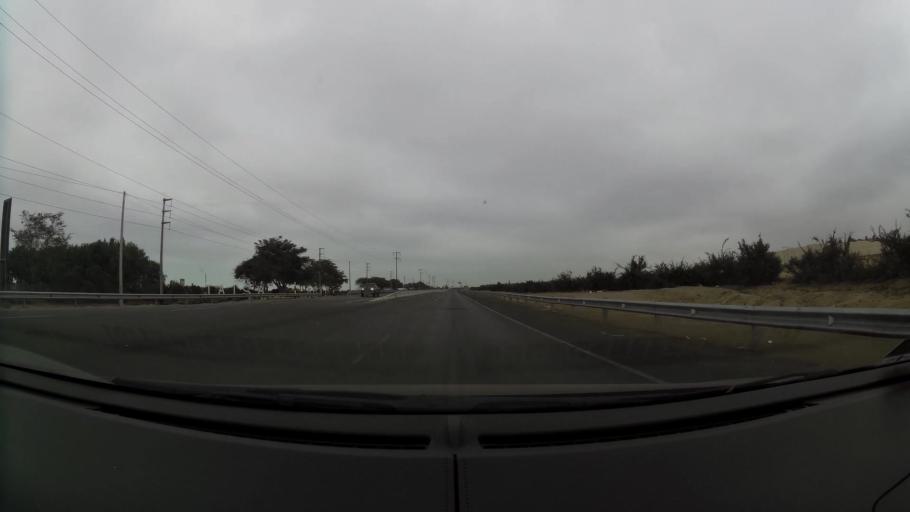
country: PE
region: La Libertad
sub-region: Viru
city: Viru
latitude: -8.3765
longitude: -78.8615
